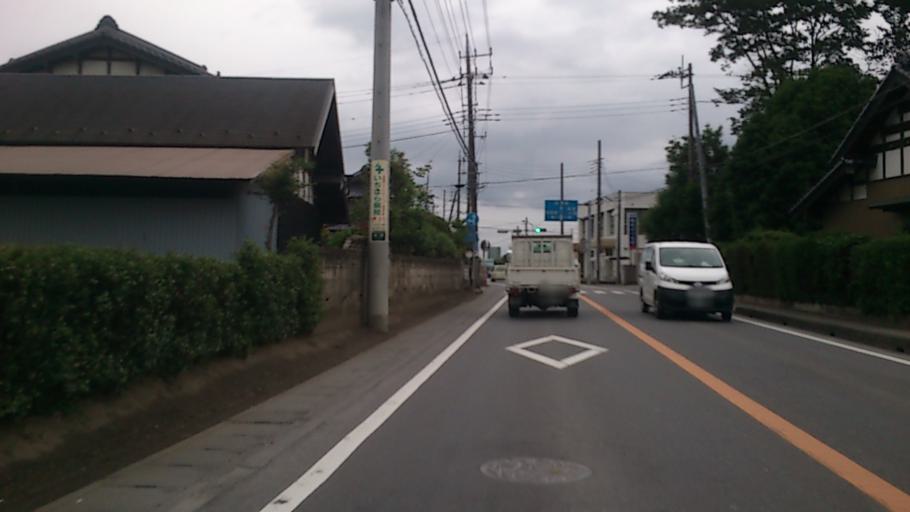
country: JP
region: Ibaraki
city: Ishige
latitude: 36.1051
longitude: 140.0494
